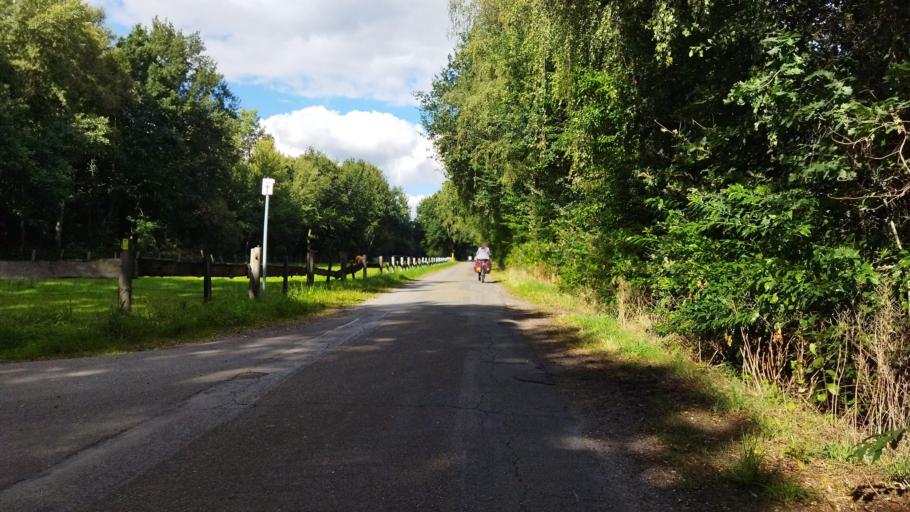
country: DE
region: Lower Saxony
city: Lingen
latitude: 52.4622
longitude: 7.3462
